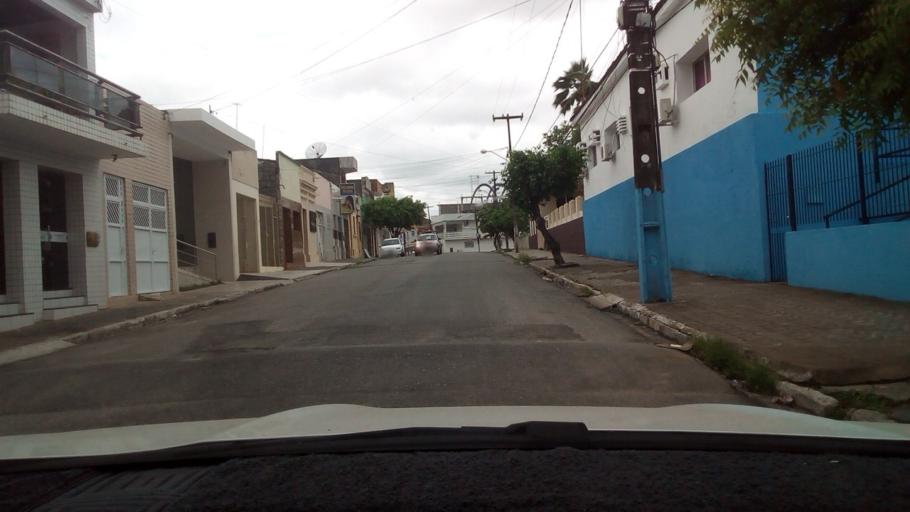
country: BR
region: Paraiba
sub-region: Guarabira
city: Guarabira
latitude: -6.8557
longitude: -35.4873
